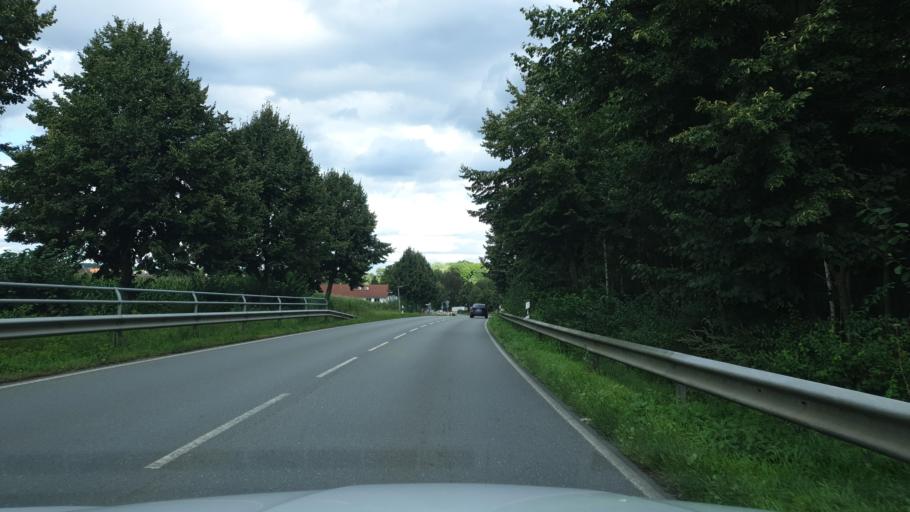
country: DE
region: North Rhine-Westphalia
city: Enger
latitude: 52.1459
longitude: 8.5777
